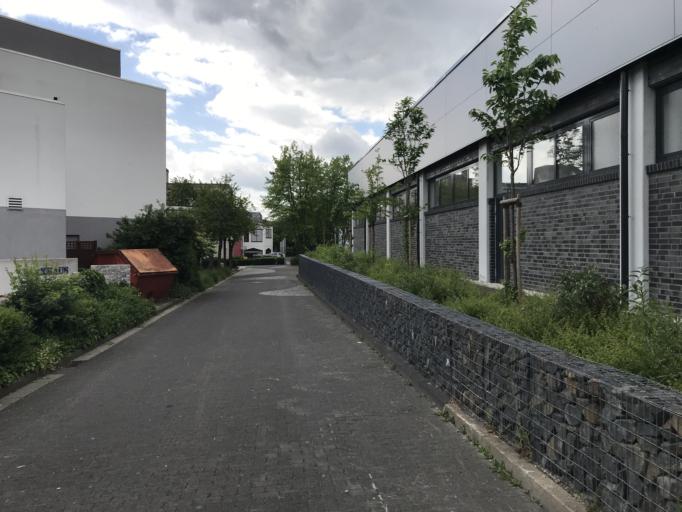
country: DE
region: Hesse
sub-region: Regierungsbezirk Kassel
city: Baunatal
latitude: 51.2549
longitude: 9.4114
